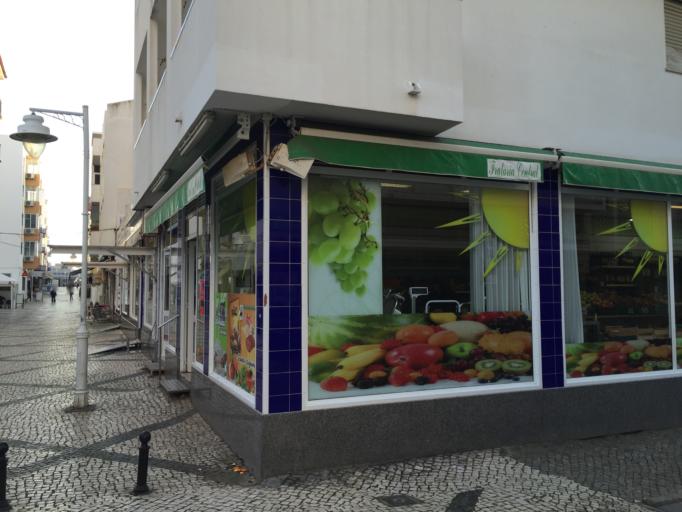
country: PT
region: Faro
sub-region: Vila Real de Santo Antonio
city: Monte Gordo
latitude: 37.1813
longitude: -7.4517
